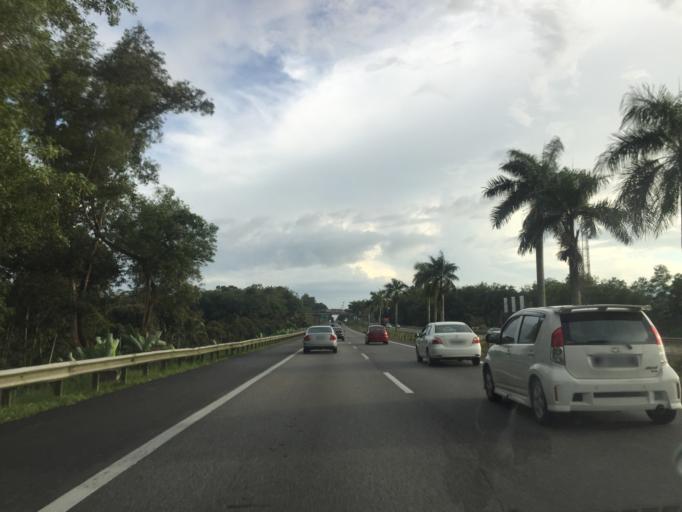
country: MY
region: Kedah
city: Gurun
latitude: 5.8440
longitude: 100.4860
